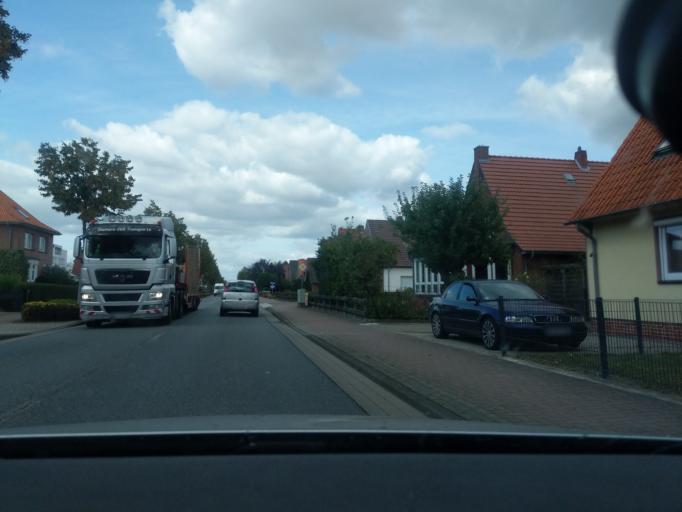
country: DE
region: Lower Saxony
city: Hoya
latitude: 52.7985
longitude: 9.1355
